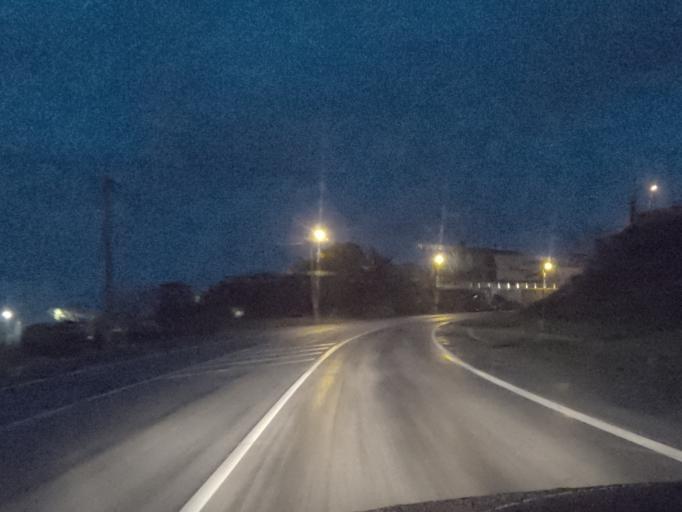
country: PT
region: Vila Real
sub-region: Peso da Regua
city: Peso da Regua
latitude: 41.1633
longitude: -7.7808
